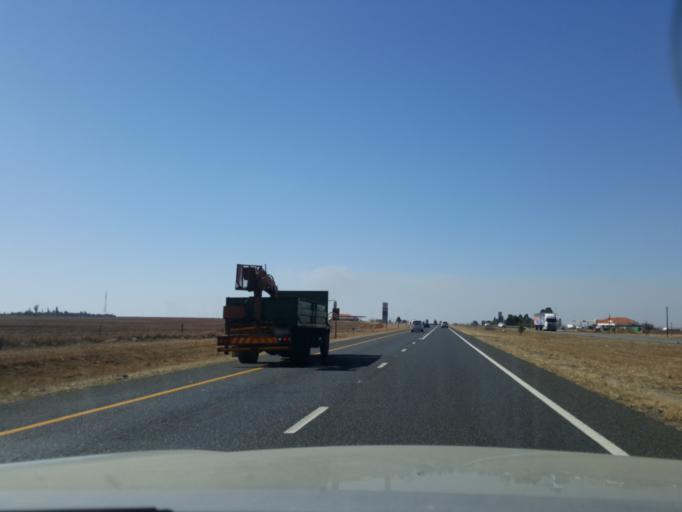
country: ZA
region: Mpumalanga
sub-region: Nkangala District Municipality
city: Delmas
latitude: -26.0479
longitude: 28.8266
